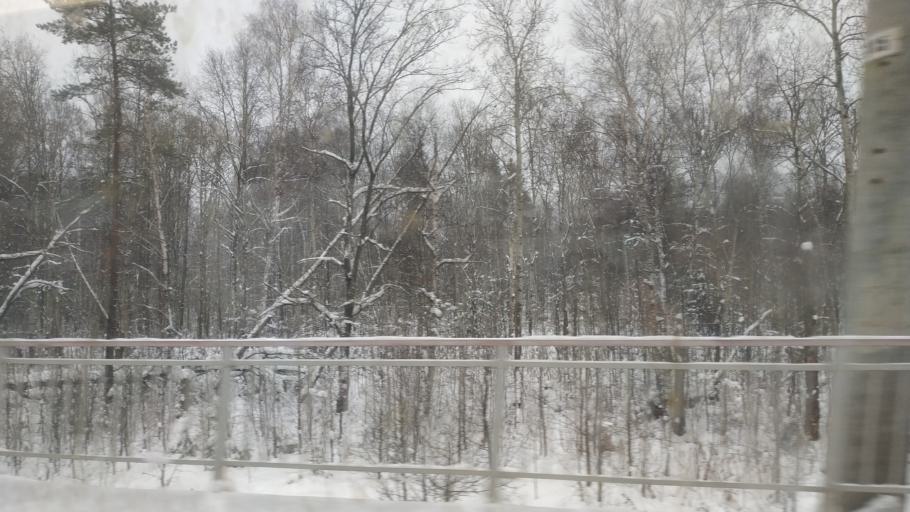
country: RU
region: Moskovskaya
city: Malyshevo
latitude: 55.5162
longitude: 38.3354
